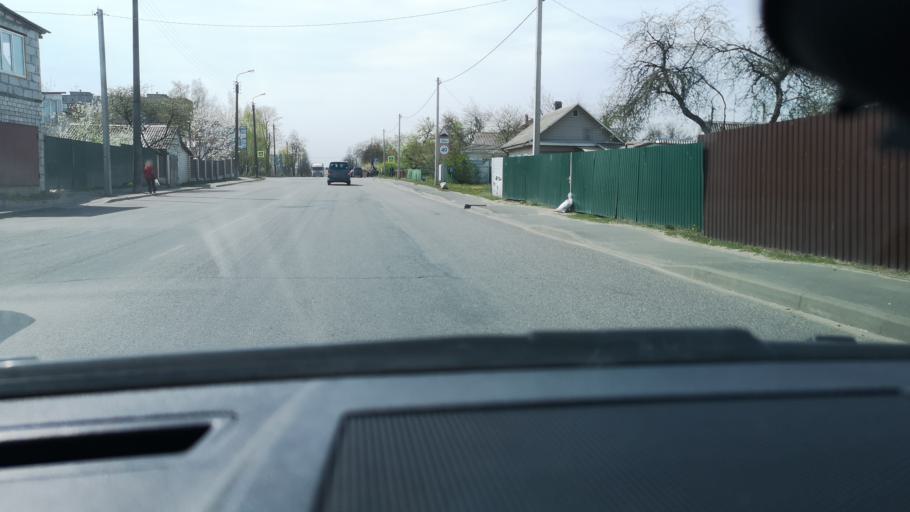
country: BY
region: Gomel
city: Gomel
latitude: 52.4135
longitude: 30.9814
